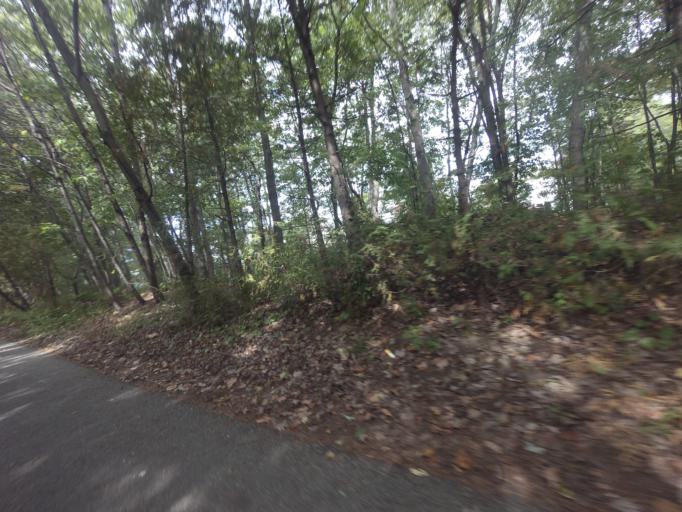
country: CA
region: Quebec
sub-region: Laurentides
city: Blainville
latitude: 45.6849
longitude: -73.8820
